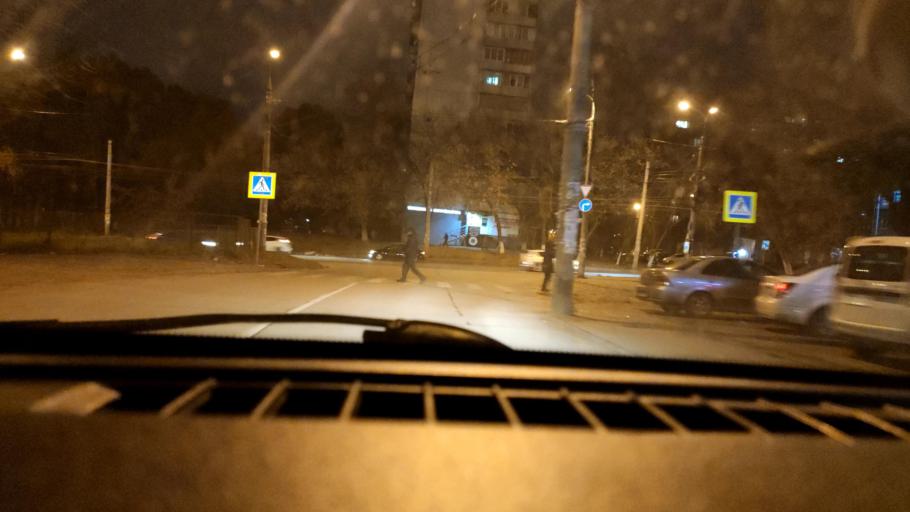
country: RU
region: Samara
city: Samara
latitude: 53.2407
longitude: 50.2368
